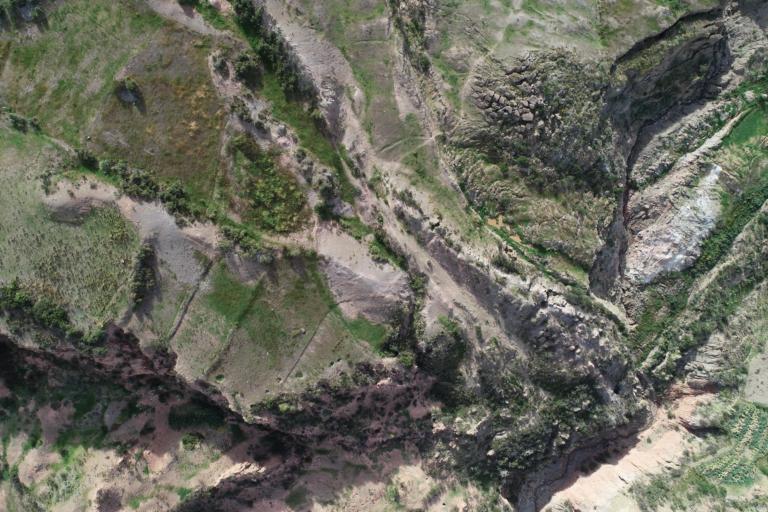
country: BO
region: La Paz
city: La Paz
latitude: -16.5517
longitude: -67.9946
